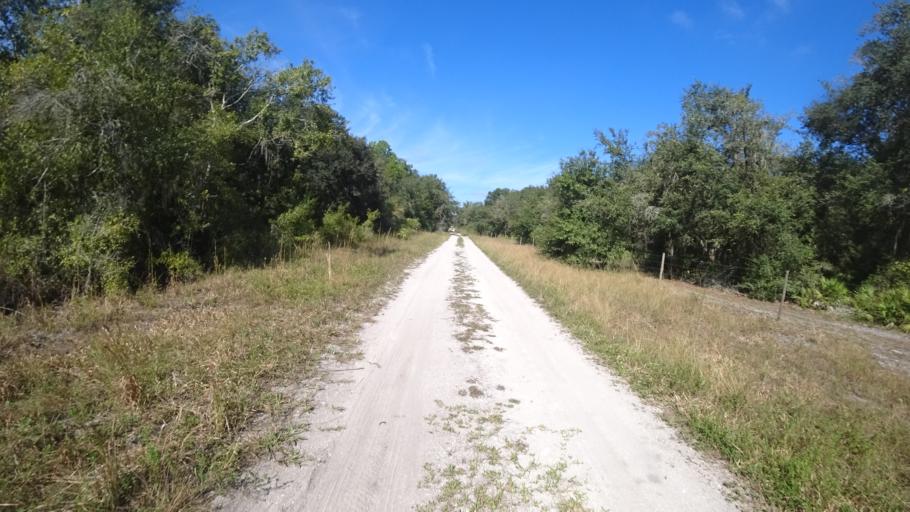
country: US
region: Florida
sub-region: DeSoto County
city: Arcadia
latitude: 27.2904
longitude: -82.0643
